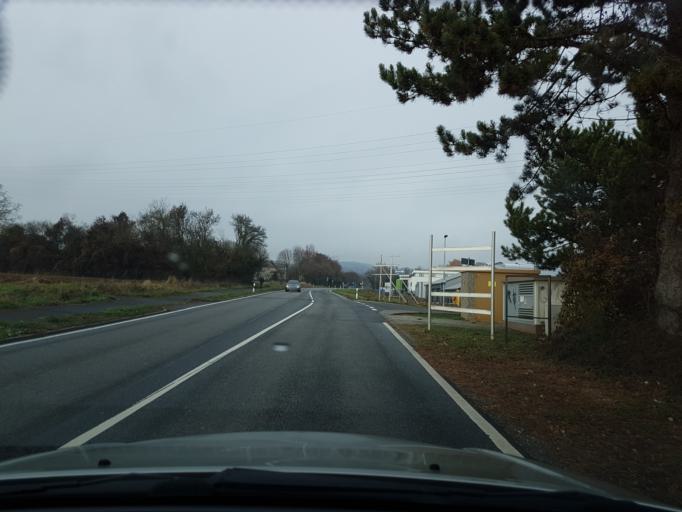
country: DE
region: Hesse
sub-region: Regierungsbezirk Darmstadt
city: Eltville
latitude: 50.0332
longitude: 8.1021
